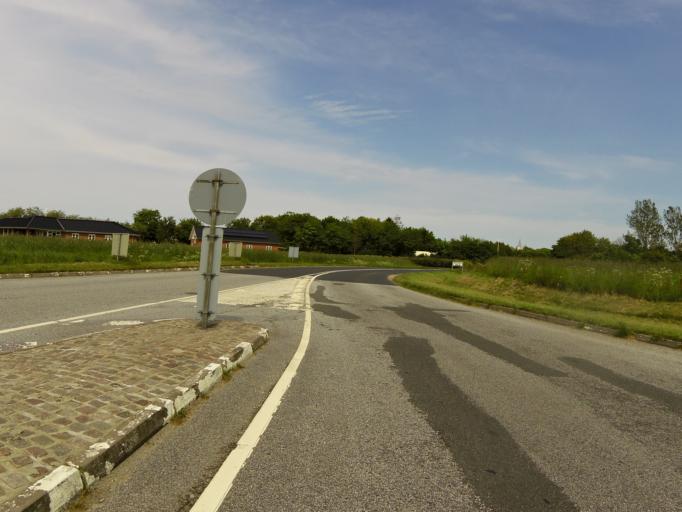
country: DK
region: South Denmark
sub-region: Esbjerg Kommune
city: Ribe
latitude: 55.2594
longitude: 8.8962
